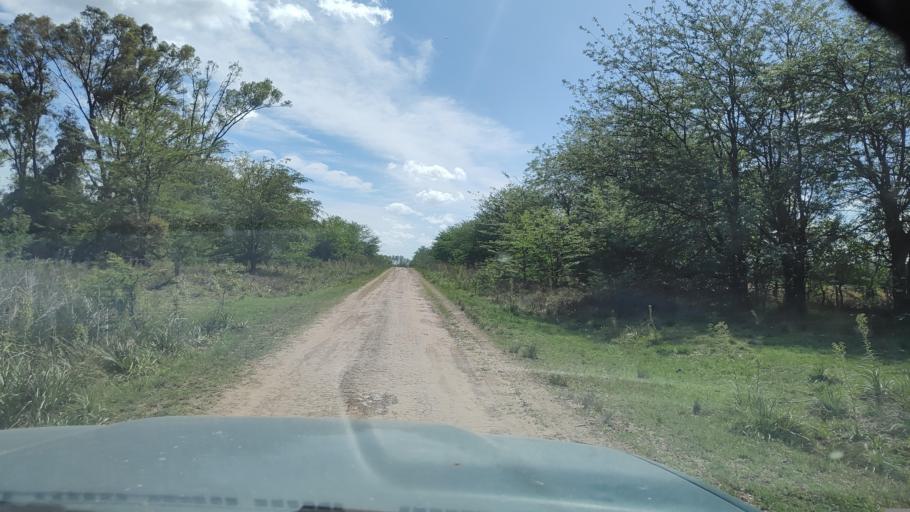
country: AR
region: Buenos Aires
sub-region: Partido de Lujan
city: Lujan
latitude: -34.5196
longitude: -59.1656
